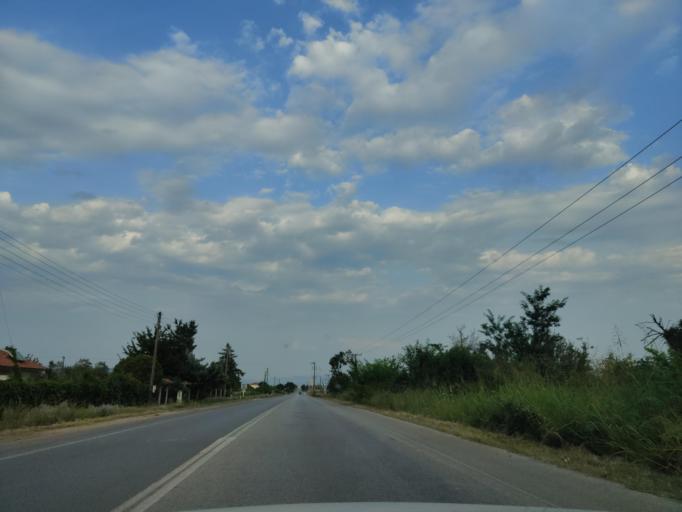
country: GR
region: East Macedonia and Thrace
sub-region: Nomos Dramas
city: Petroussa
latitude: 41.1671
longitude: 24.0531
